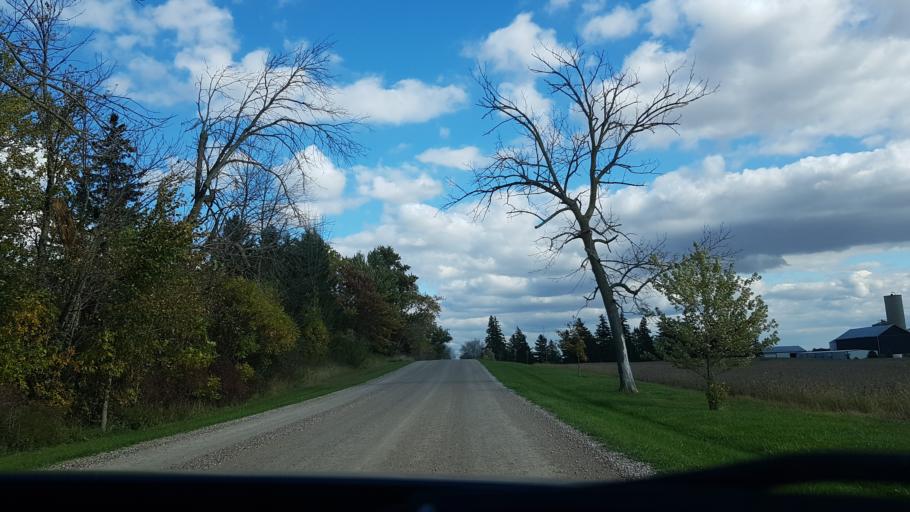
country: CA
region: Ontario
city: South Huron
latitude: 43.1111
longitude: -81.6387
